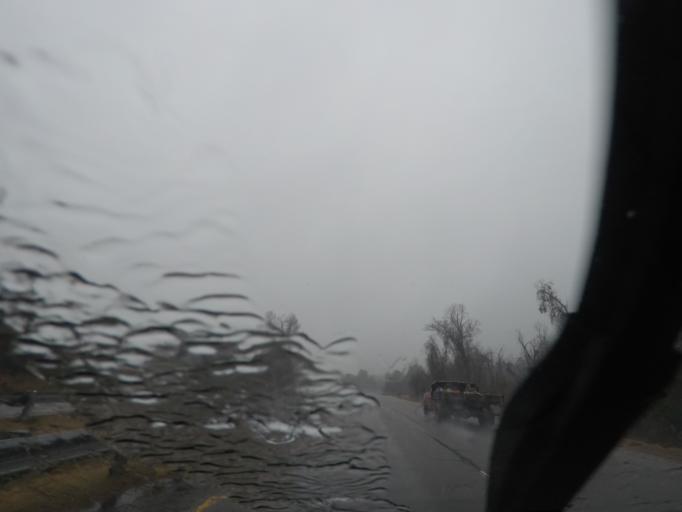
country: US
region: North Carolina
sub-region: Moore County
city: Southern Pines
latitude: 35.1823
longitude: -79.3950
